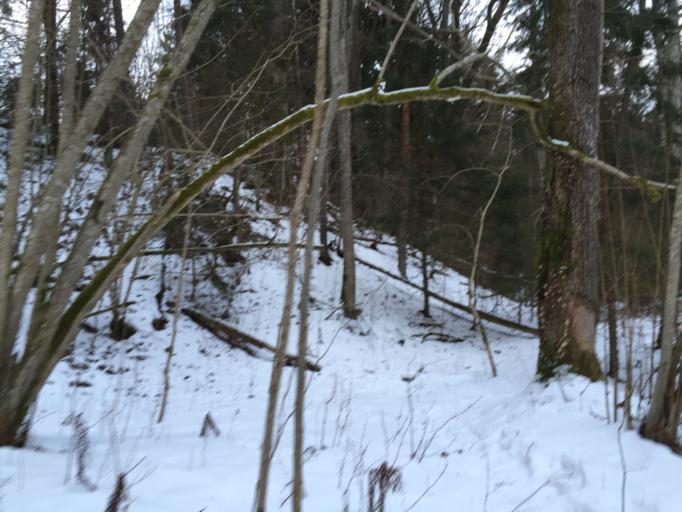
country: LV
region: Seja
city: Loja
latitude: 57.1358
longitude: 24.6716
